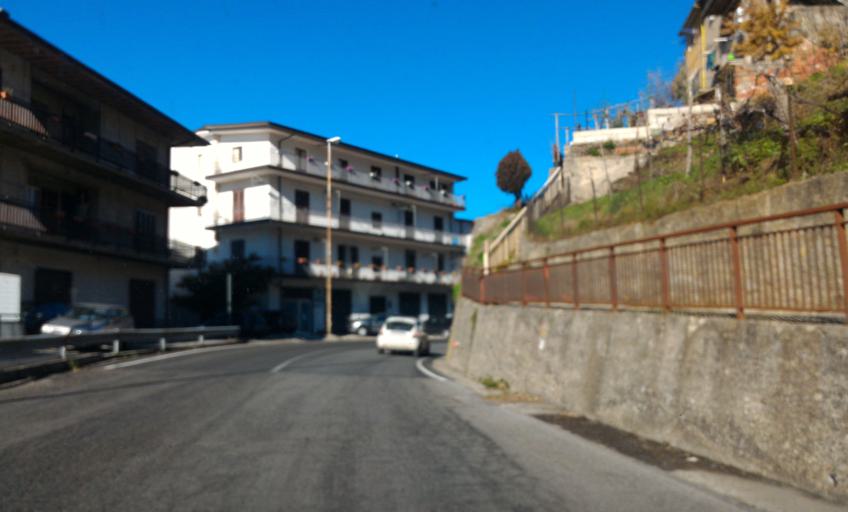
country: IT
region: Calabria
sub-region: Provincia di Cosenza
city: Spezzano della Sila
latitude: 39.2983
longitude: 16.3425
